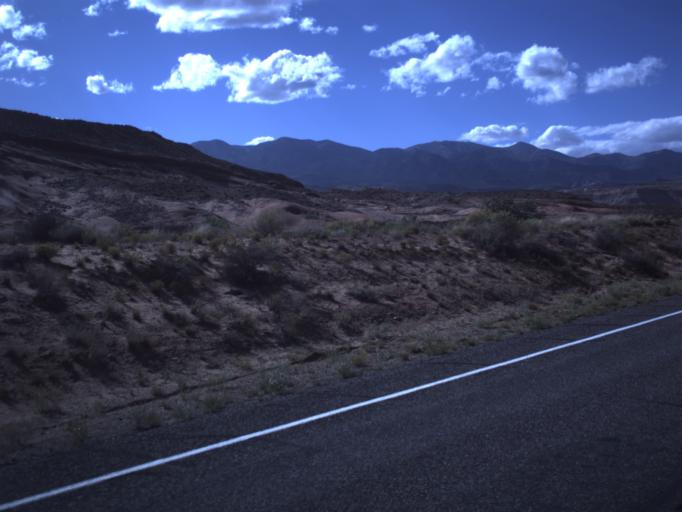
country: US
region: Utah
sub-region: Wayne County
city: Loa
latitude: 38.0583
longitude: -110.5941
